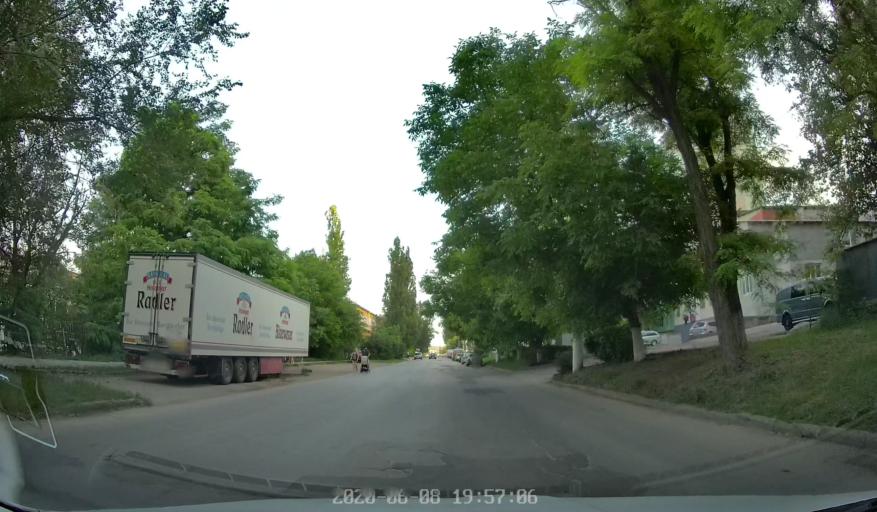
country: MD
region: Chisinau
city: Chisinau
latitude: 47.0178
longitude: 28.8827
